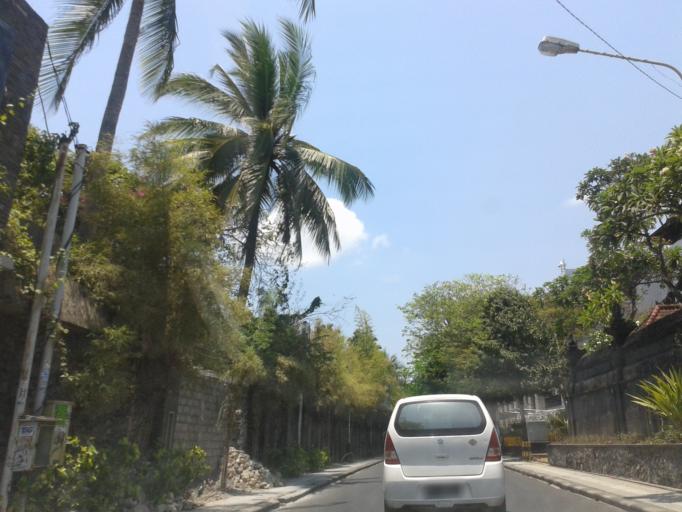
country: ID
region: Bali
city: Kuta
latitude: -8.7091
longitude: 115.1670
